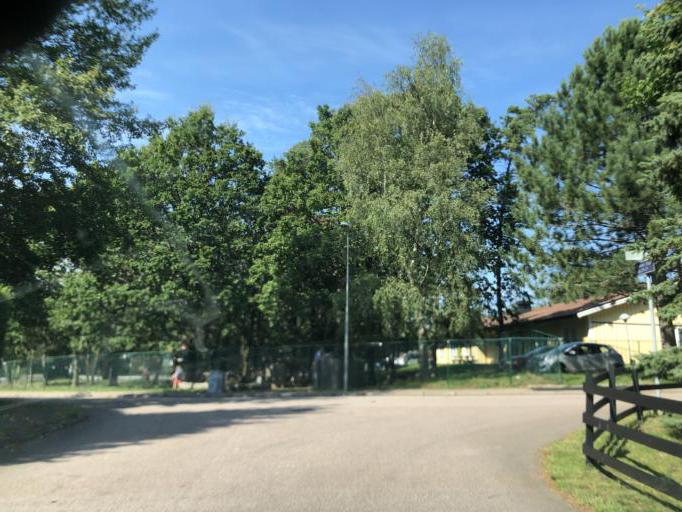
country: SE
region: Vaestra Goetaland
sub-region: Goteborg
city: Goeteborg
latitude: 57.7577
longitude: 11.9690
